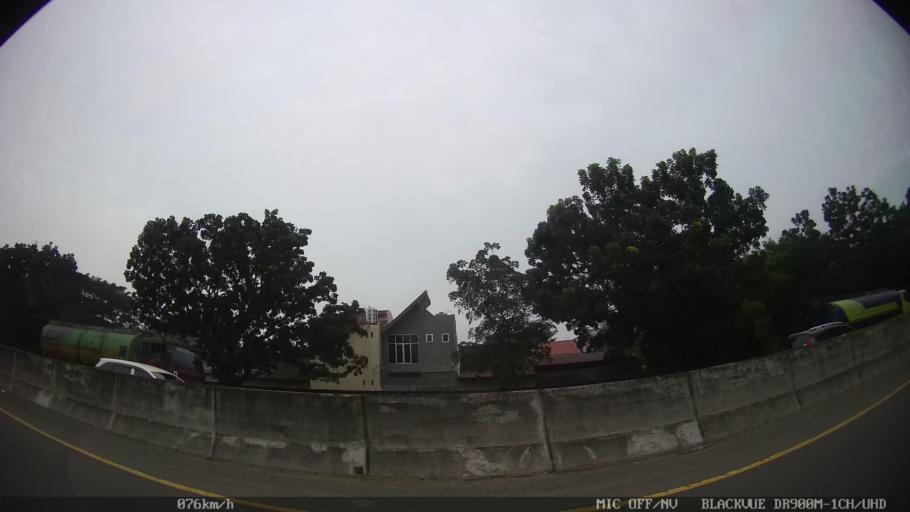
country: ID
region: North Sumatra
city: Medan
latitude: 3.5582
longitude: 98.7254
